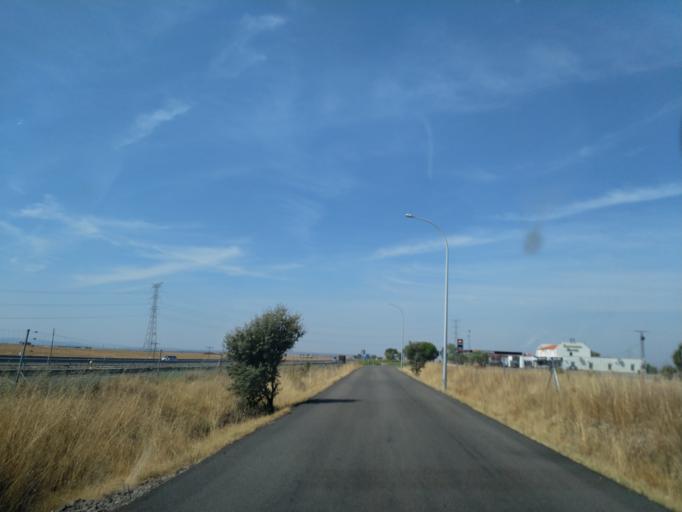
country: ES
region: Castille-La Mancha
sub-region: Province of Toledo
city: Caleruela
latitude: 39.8953
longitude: -5.3302
